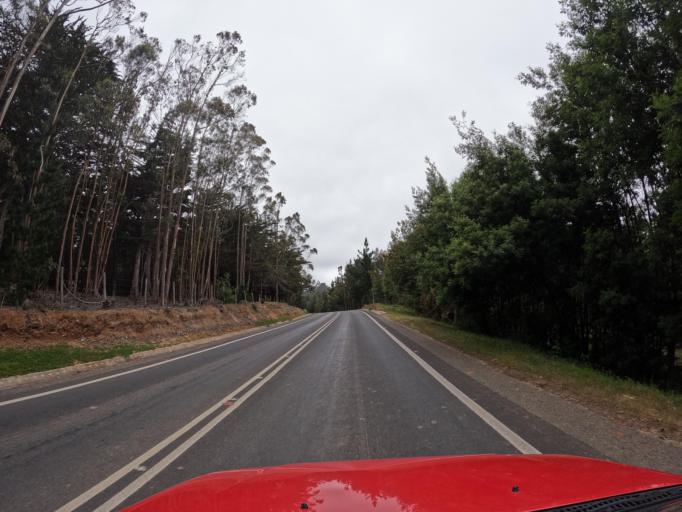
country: CL
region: O'Higgins
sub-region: Provincia de Colchagua
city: Santa Cruz
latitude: -34.5933
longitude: -72.0160
